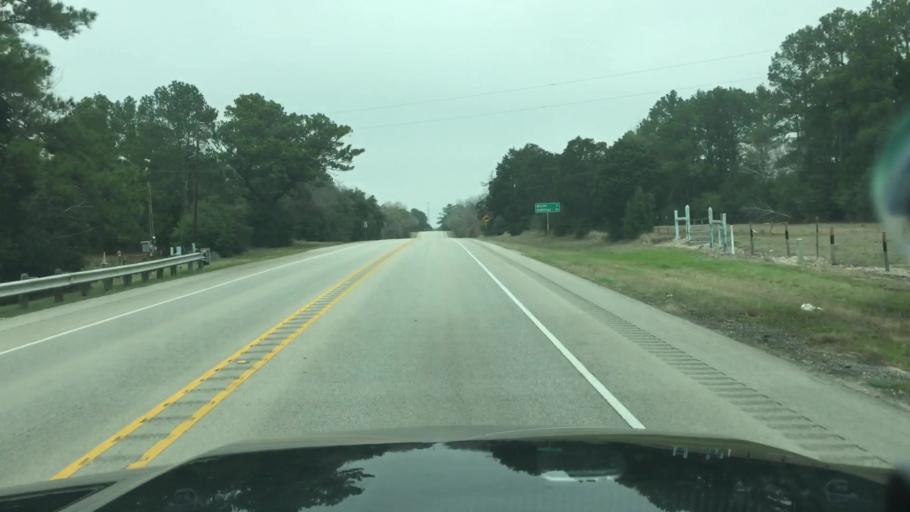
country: US
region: Texas
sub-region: Fayette County
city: La Grange
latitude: 30.0015
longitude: -96.8923
